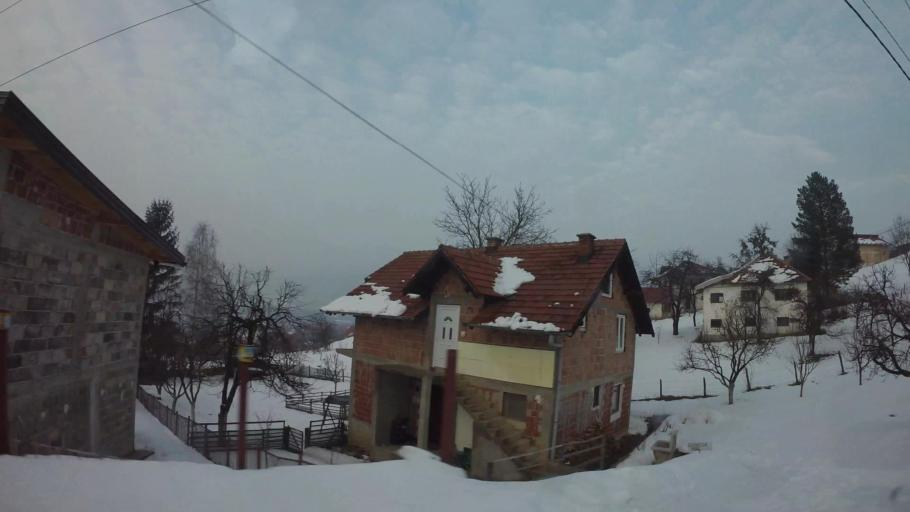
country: BA
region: Federation of Bosnia and Herzegovina
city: Hotonj
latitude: 43.8911
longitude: 18.3649
